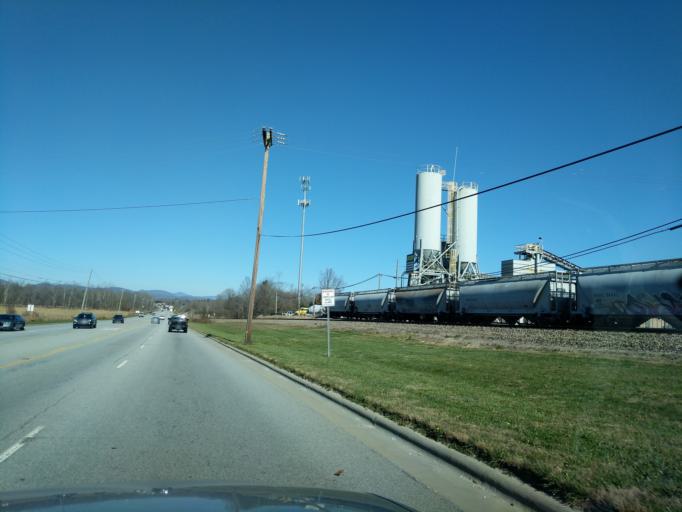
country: US
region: North Carolina
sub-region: Henderson County
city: Fletcher
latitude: 35.4151
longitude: -82.5074
